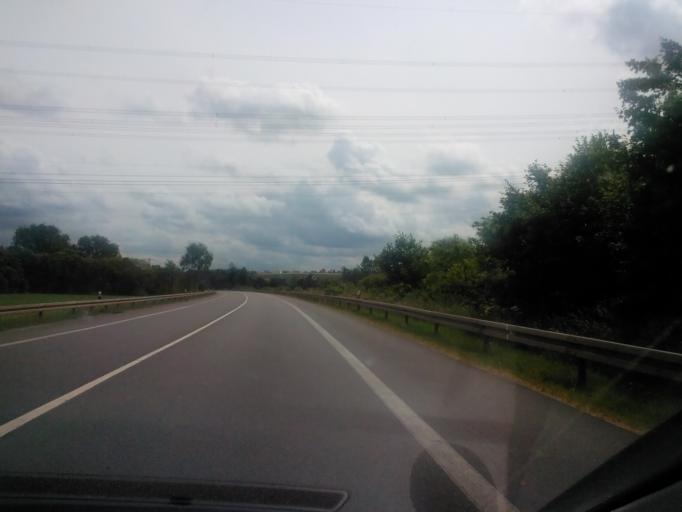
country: DE
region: Saarland
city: Lebach
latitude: 49.4127
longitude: 6.9237
